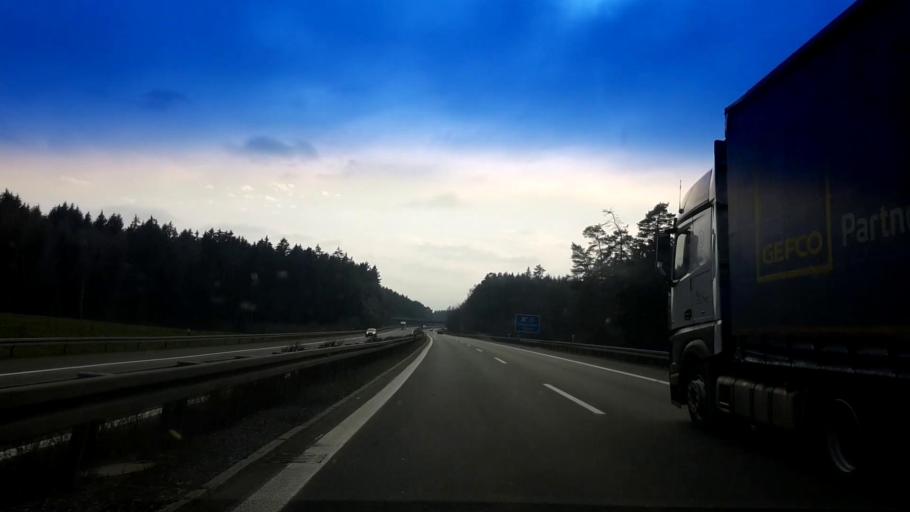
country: DE
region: Bavaria
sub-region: Upper Franconia
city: Stadelhofen
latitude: 50.0064
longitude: 11.2277
